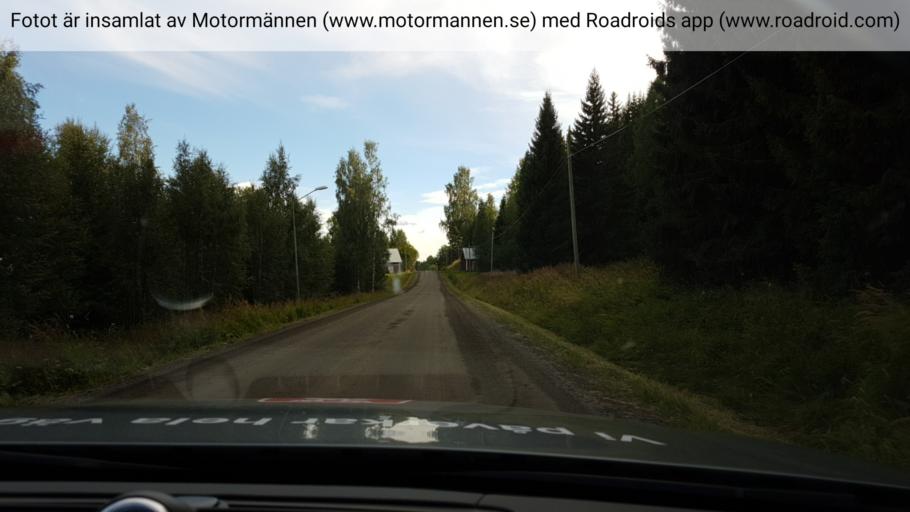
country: SE
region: Jaemtland
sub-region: Stroemsunds Kommun
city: Stroemsund
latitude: 64.0422
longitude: 15.8100
